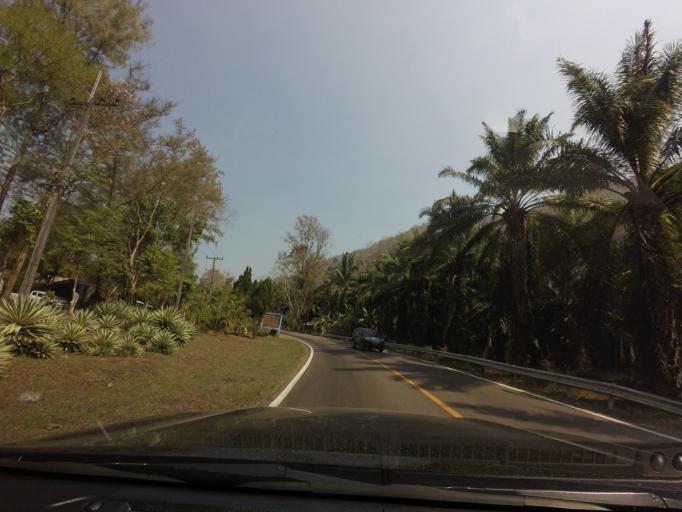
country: TH
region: Kanchanaburi
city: Thong Pha Phum
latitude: 14.7472
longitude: 98.5786
